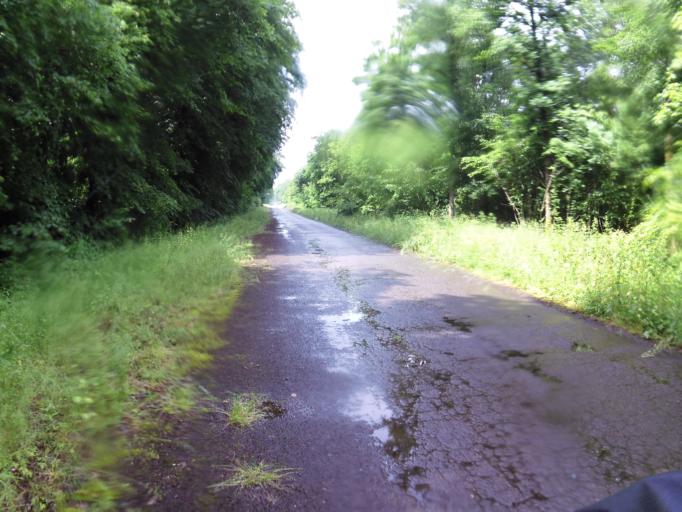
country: FR
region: Champagne-Ardenne
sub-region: Departement de la Marne
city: Sermaize-les-Bains
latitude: 48.7467
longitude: 4.9738
